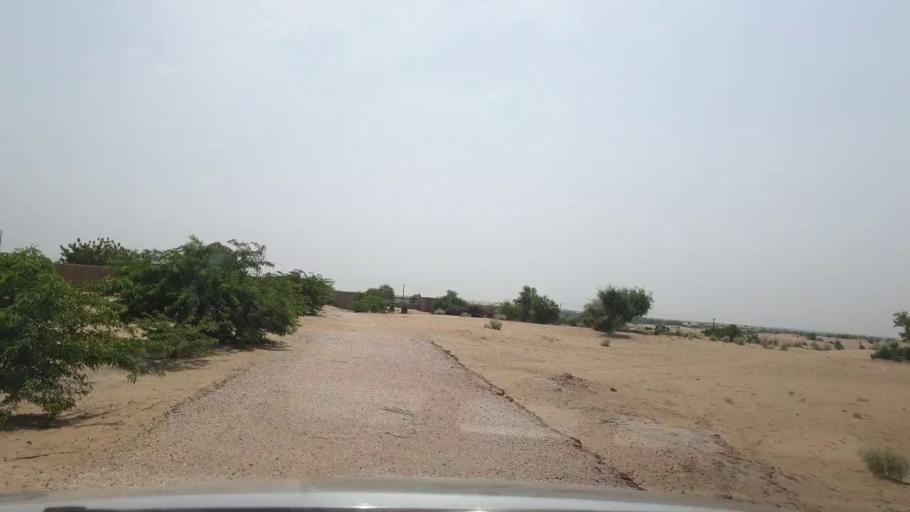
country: PK
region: Sindh
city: Pano Aqil
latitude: 27.6082
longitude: 69.1536
